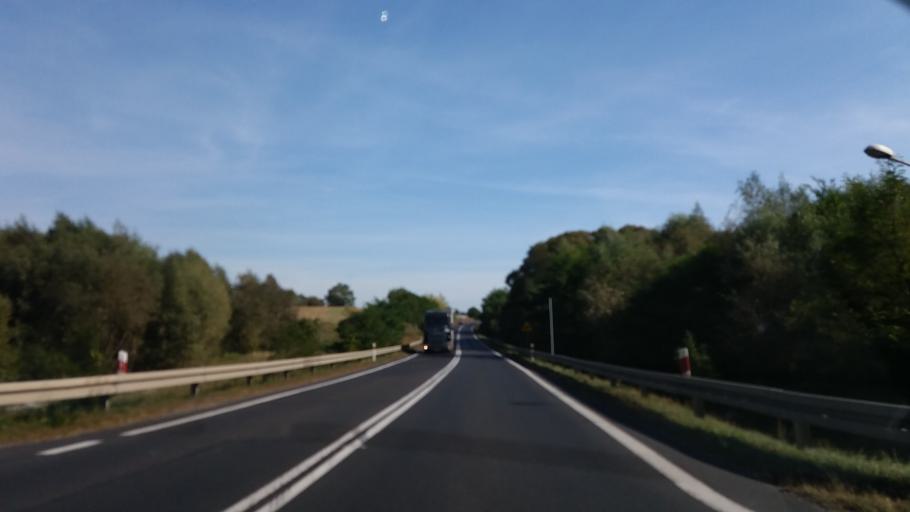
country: PL
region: Greater Poland Voivodeship
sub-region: Powiat miedzychodzki
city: Kwilcz
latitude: 52.5527
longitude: 16.0976
